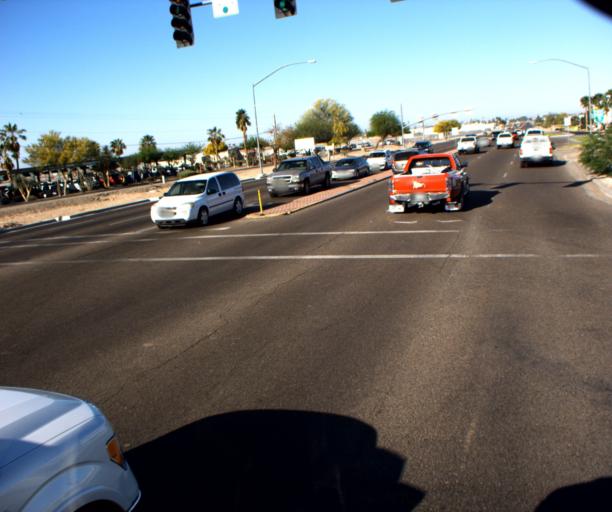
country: US
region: Arizona
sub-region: Yuma County
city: Yuma
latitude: 32.6695
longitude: -114.5987
